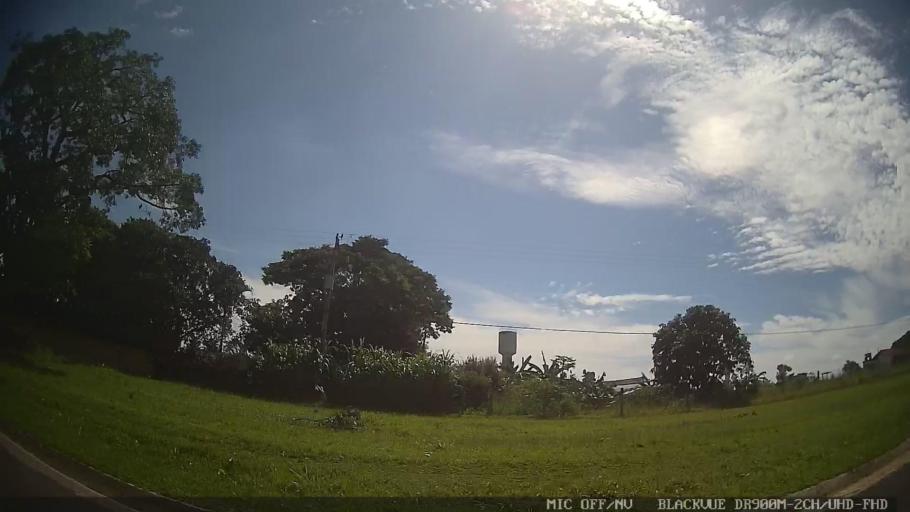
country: BR
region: Sao Paulo
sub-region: Tiete
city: Tiete
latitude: -23.1684
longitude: -47.6444
